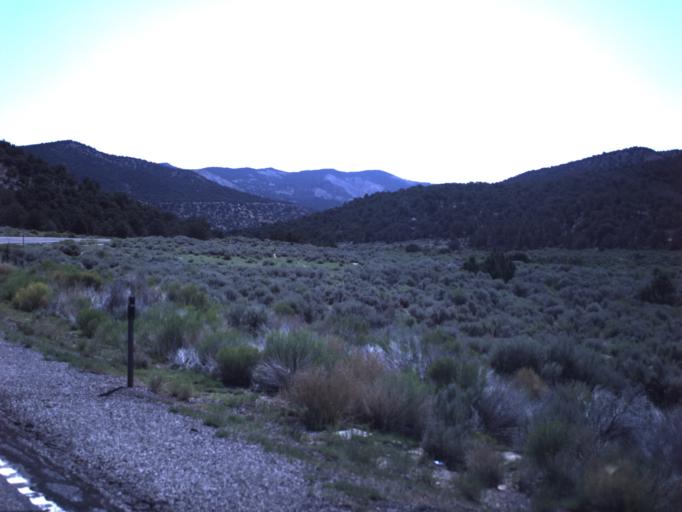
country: US
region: Utah
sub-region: Wayne County
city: Loa
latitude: 38.6721
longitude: -111.4184
